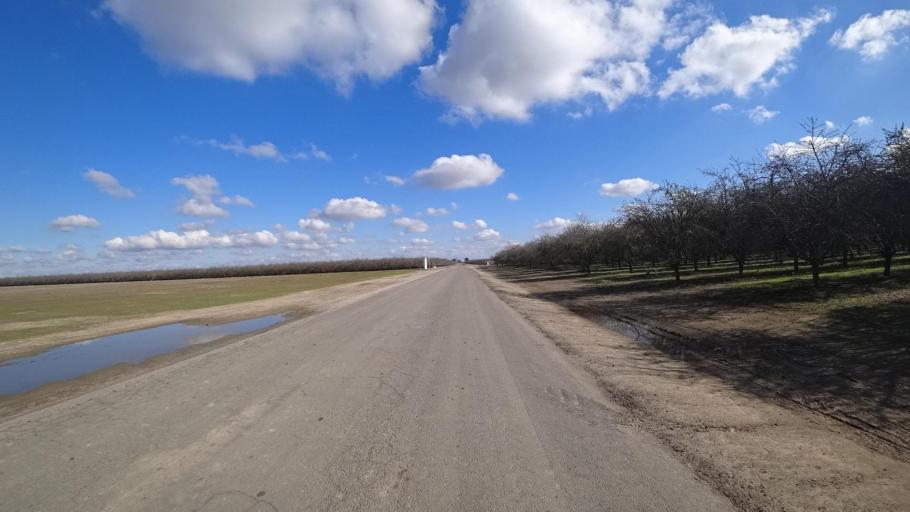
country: US
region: California
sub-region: Kern County
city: Delano
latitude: 35.7466
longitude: -119.3585
